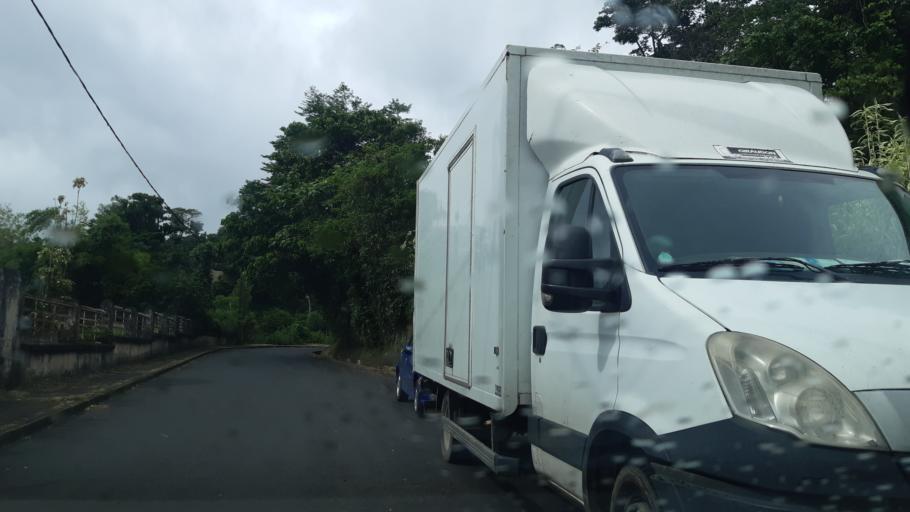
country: GP
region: Guadeloupe
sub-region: Guadeloupe
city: Saint-Claude
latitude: 16.0444
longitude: -61.6925
